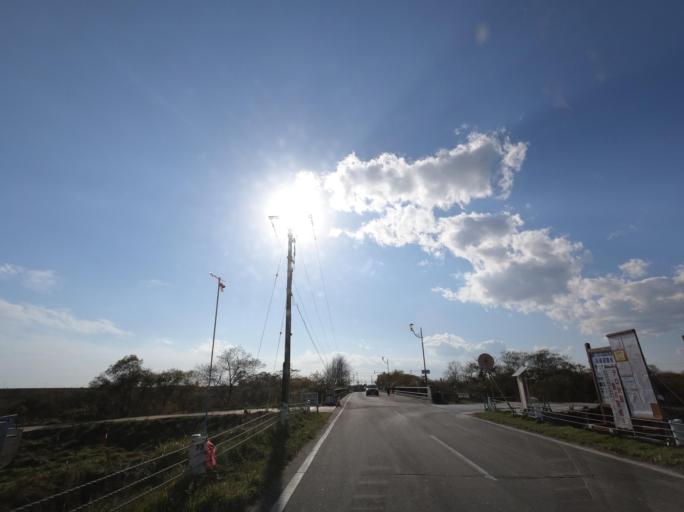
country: JP
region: Hokkaido
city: Kushiro
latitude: 43.0396
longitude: 144.3170
